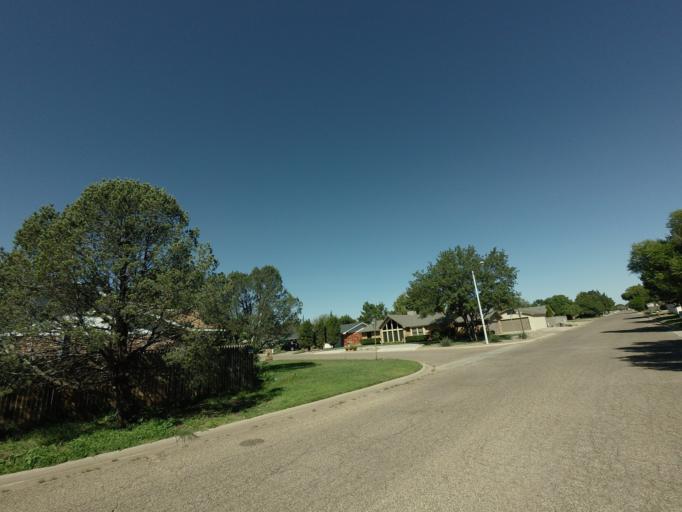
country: US
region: New Mexico
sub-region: Curry County
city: Clovis
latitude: 34.4213
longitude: -103.1743
